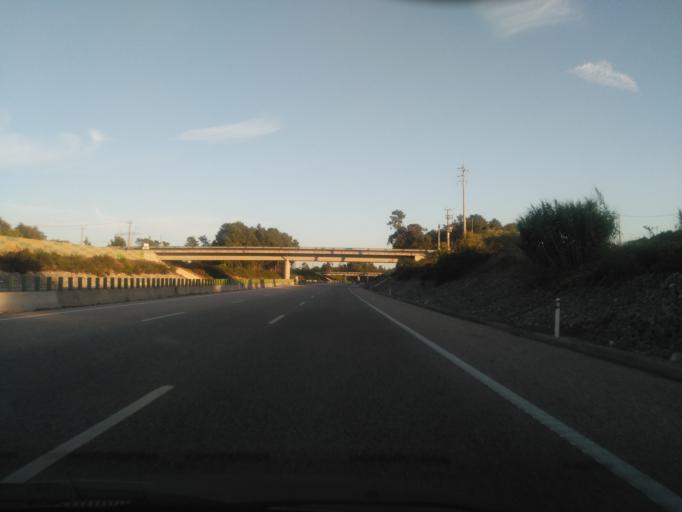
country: PT
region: Leiria
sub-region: Pombal
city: Lourical
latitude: 39.9678
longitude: -8.7797
